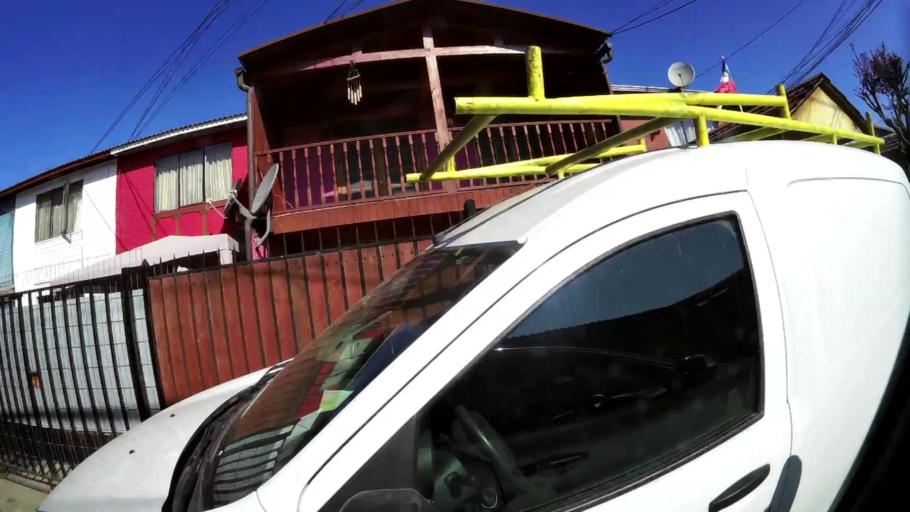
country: CL
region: Santiago Metropolitan
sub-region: Provincia de Santiago
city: Lo Prado
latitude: -33.4886
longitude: -70.7702
